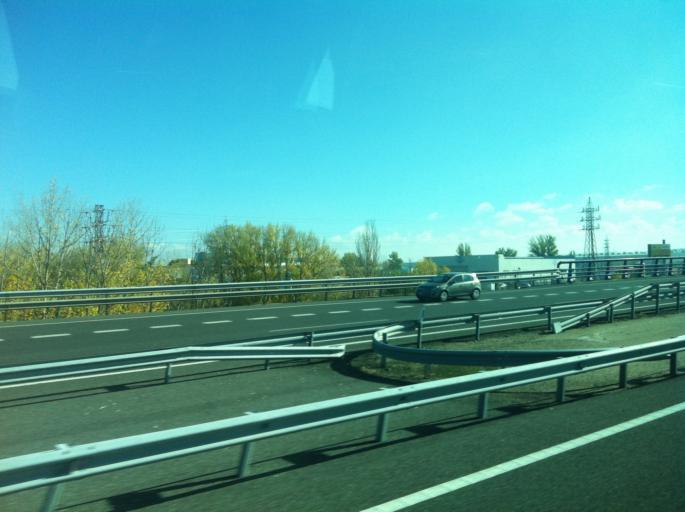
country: ES
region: Castille and Leon
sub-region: Provincia de Burgos
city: Villalba de Duero
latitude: 41.6681
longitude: -3.7282
